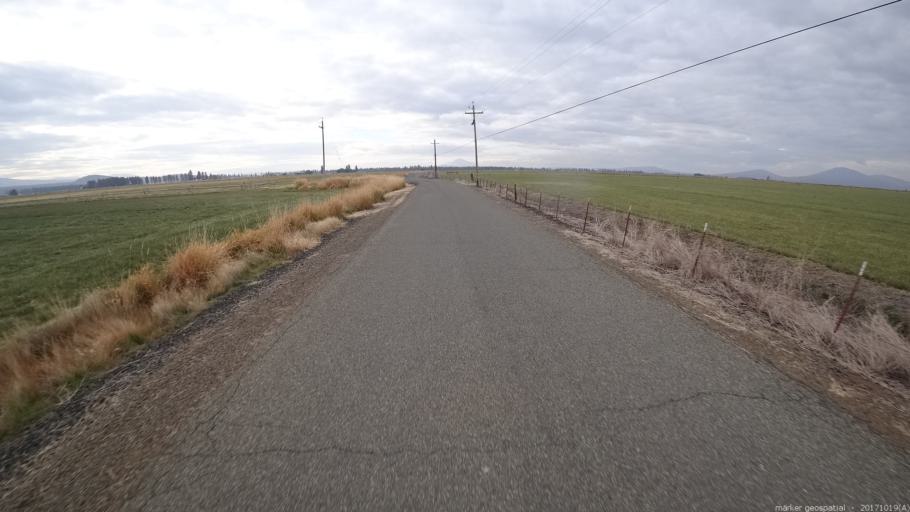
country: US
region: California
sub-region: Shasta County
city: Burney
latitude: 41.0882
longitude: -121.3654
